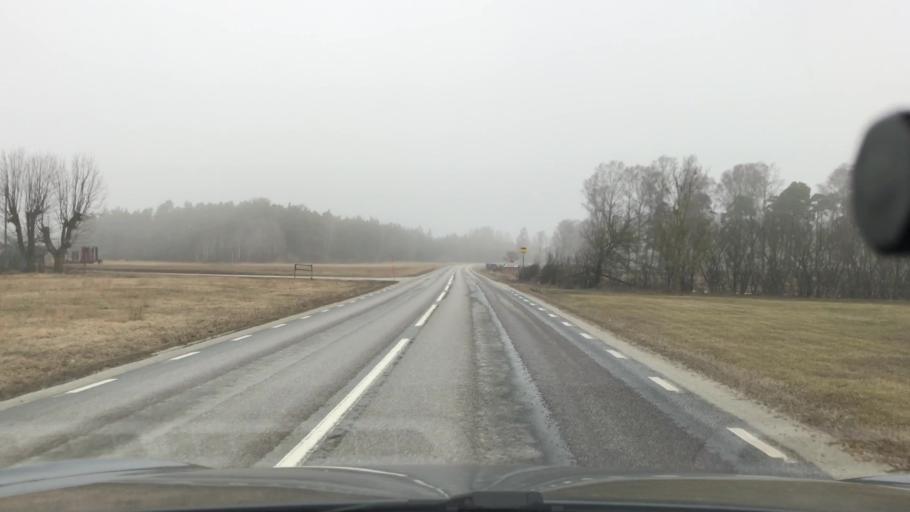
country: SE
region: Gotland
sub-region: Gotland
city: Hemse
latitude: 57.3237
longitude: 18.3836
